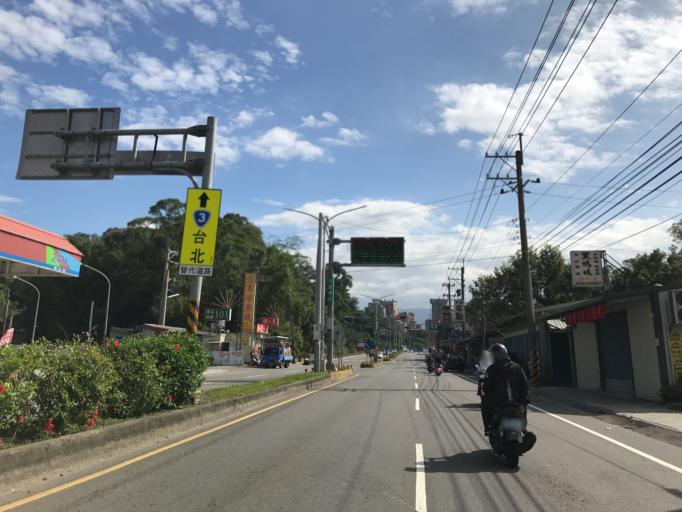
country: TW
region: Taiwan
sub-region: Hsinchu
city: Zhubei
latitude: 24.7257
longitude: 121.1304
